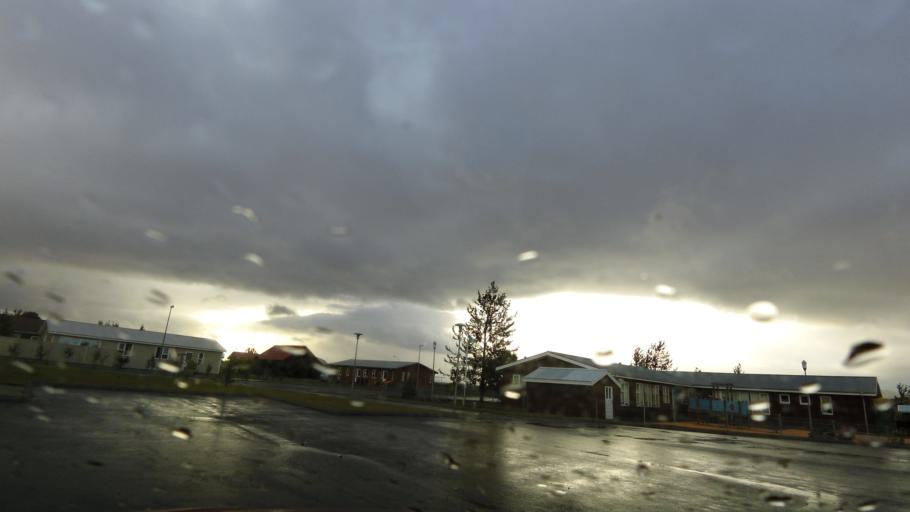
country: IS
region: West
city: Borgarnes
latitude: 64.3815
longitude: -21.8406
